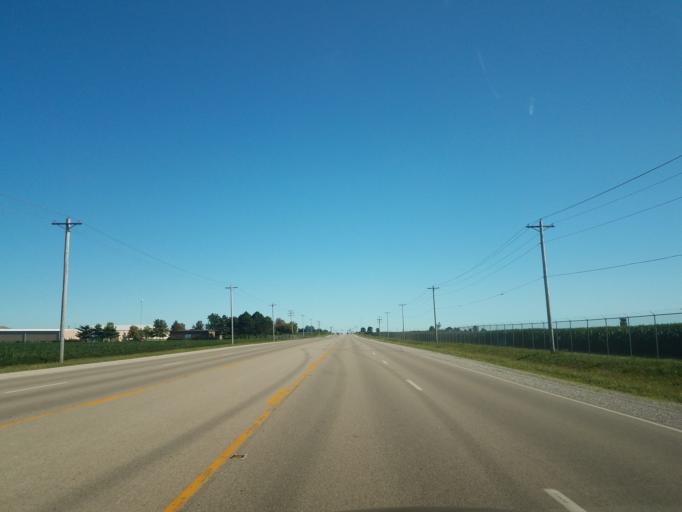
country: US
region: Illinois
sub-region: McLean County
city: Downs
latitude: 40.4809
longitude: -88.9024
